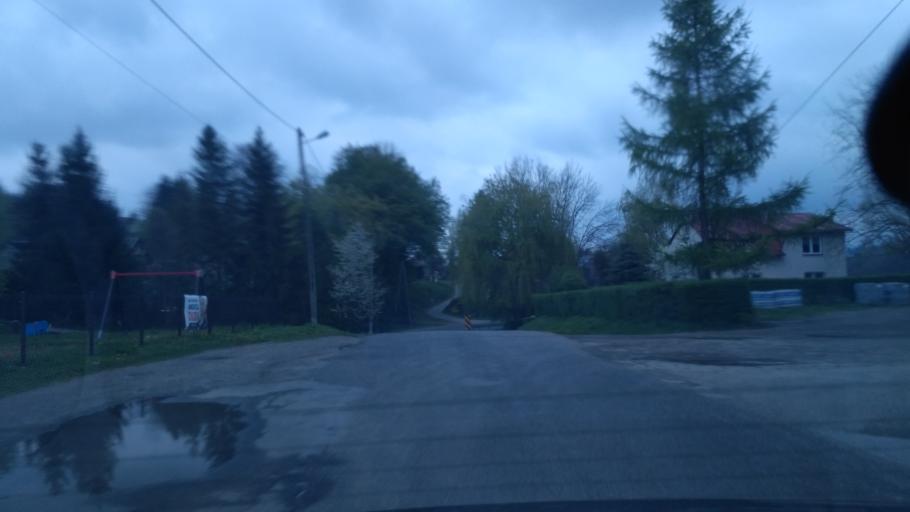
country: PL
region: Subcarpathian Voivodeship
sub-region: Powiat sanocki
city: Sanok
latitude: 49.6324
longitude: 22.2778
